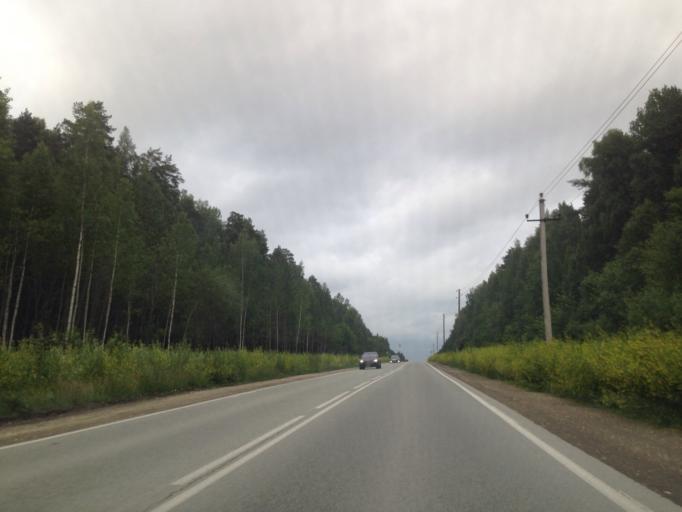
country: RU
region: Sverdlovsk
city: Istok
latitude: 56.8394
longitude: 60.7720
